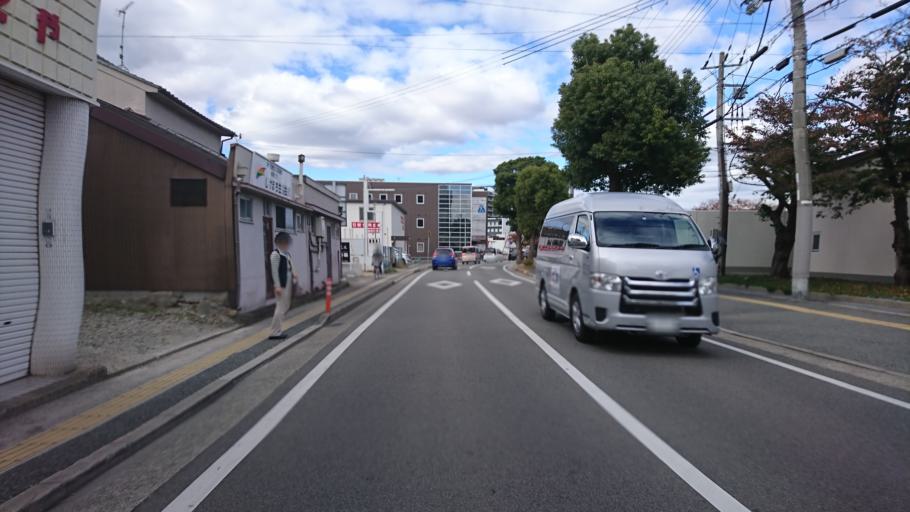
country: JP
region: Hyogo
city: Kakogawacho-honmachi
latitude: 34.7683
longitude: 134.8355
